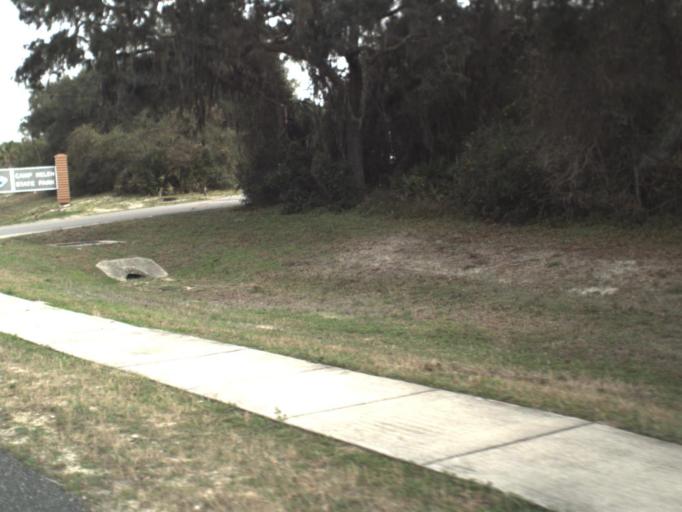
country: US
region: Florida
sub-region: Bay County
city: Laguna Beach
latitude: 30.2757
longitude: -85.9909
